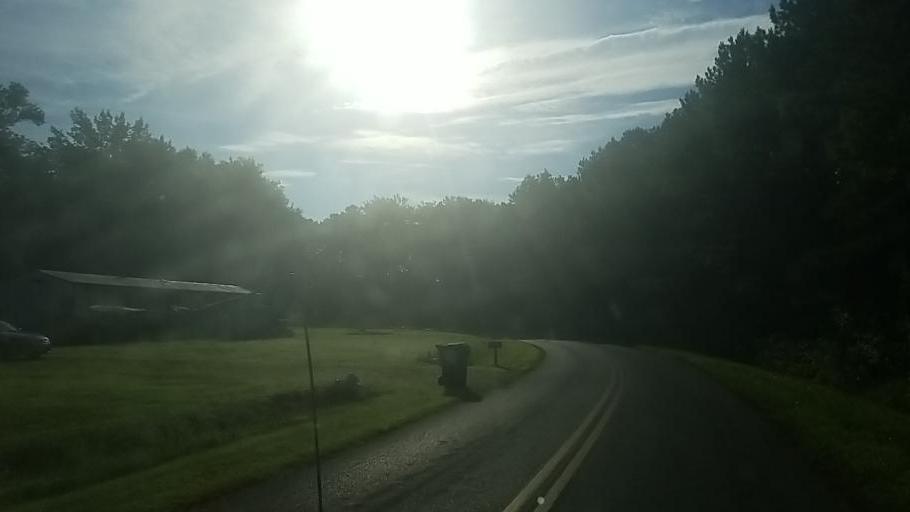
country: US
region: Maryland
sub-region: Worcester County
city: West Ocean City
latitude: 38.3125
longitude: -75.1590
